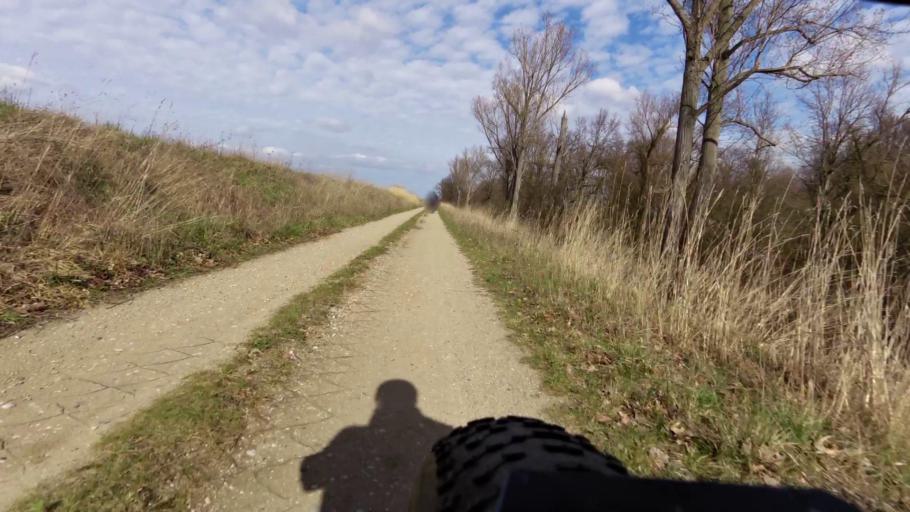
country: DE
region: Brandenburg
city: Reitwein
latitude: 52.4515
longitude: 14.5975
